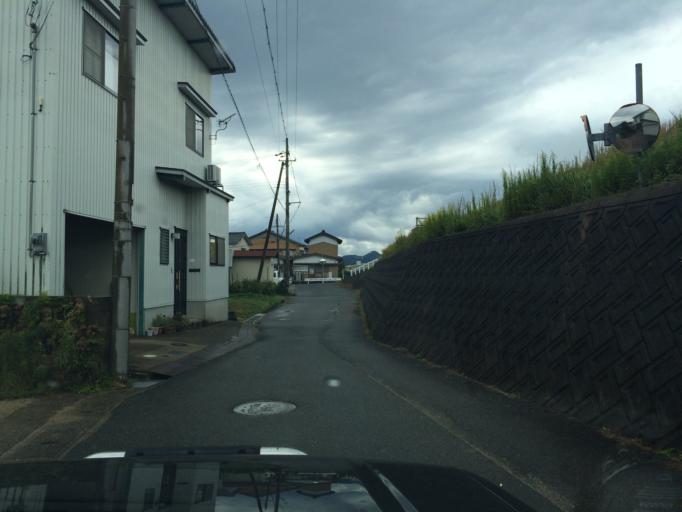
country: JP
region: Hyogo
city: Toyooka
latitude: 35.5244
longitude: 134.8265
